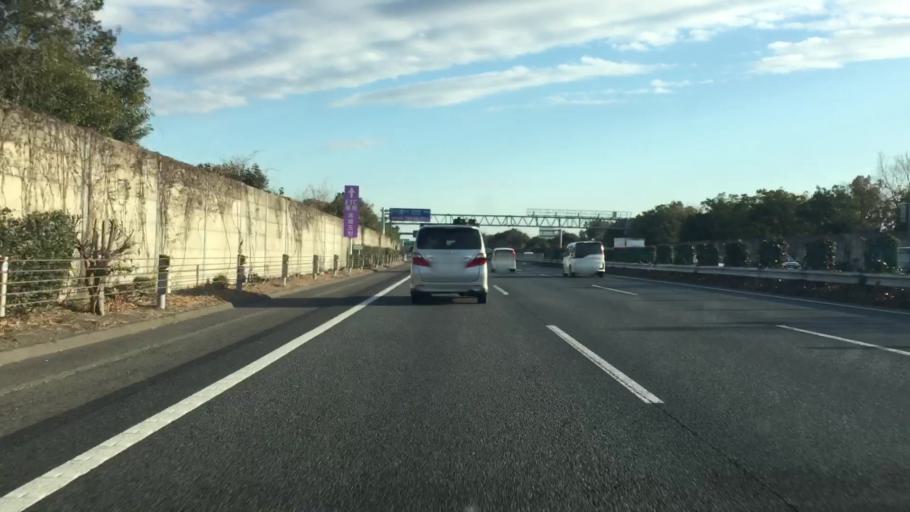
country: JP
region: Gunma
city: Takasaki
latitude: 36.3285
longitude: 139.0657
